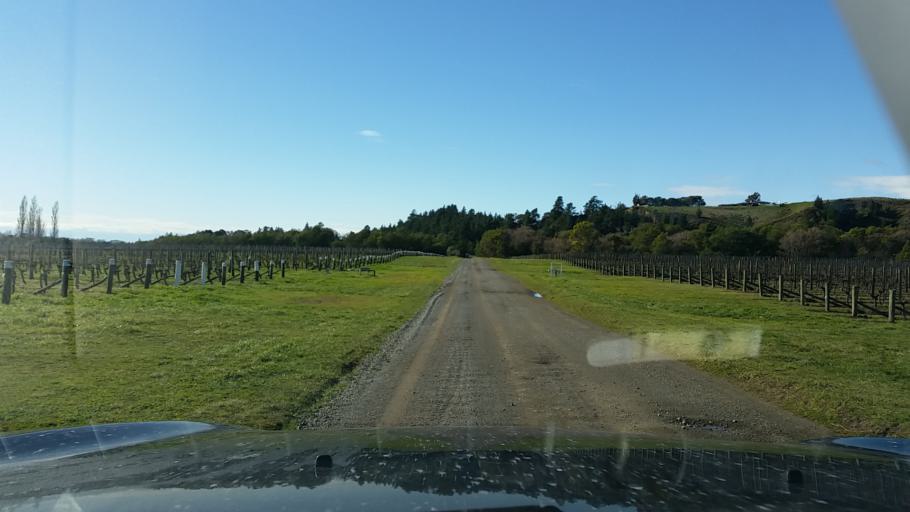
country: NZ
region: Marlborough
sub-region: Marlborough District
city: Blenheim
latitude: -41.5297
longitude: 173.7968
